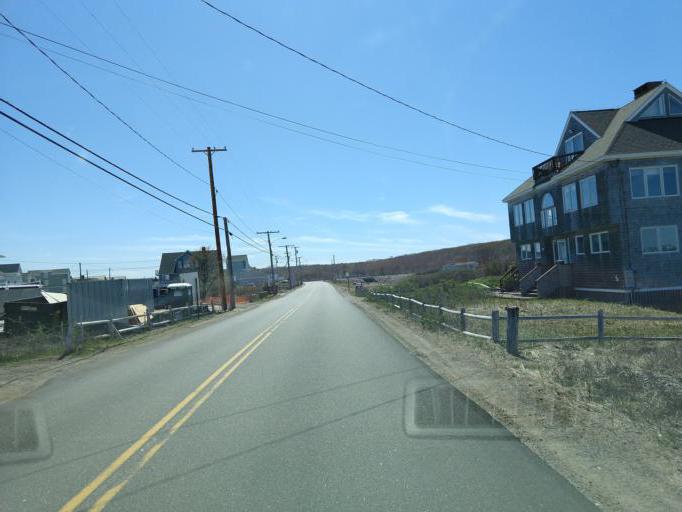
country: US
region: Maine
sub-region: York County
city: Old Orchard Beach
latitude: 43.4375
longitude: -70.3675
